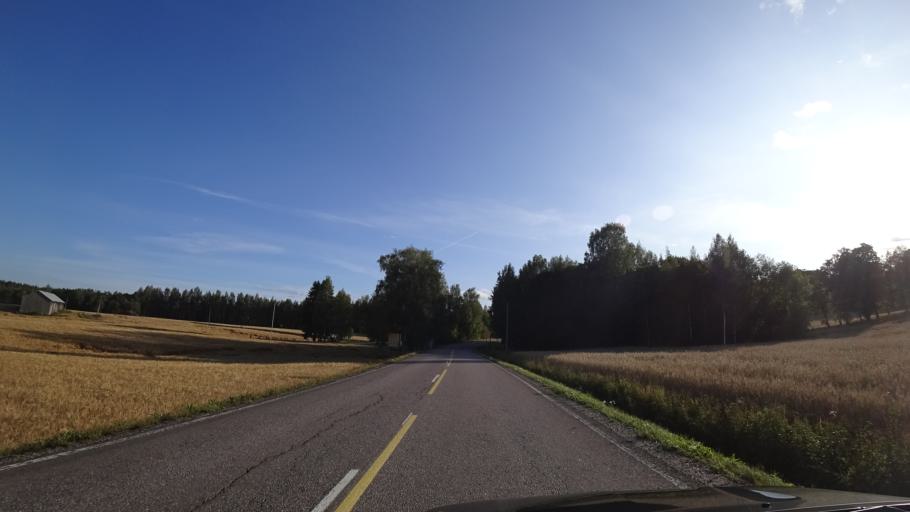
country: FI
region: Paijanne Tavastia
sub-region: Lahti
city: Asikkala
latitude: 61.1805
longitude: 25.3789
